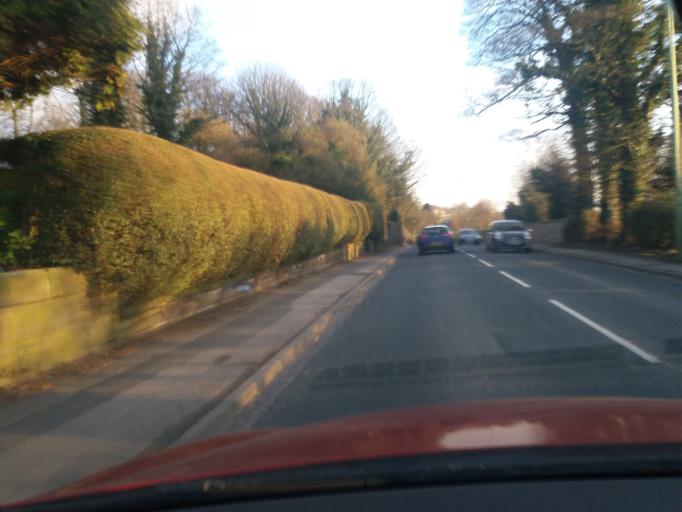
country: GB
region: England
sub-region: Lancashire
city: Chorley
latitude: 53.6761
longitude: -2.6161
